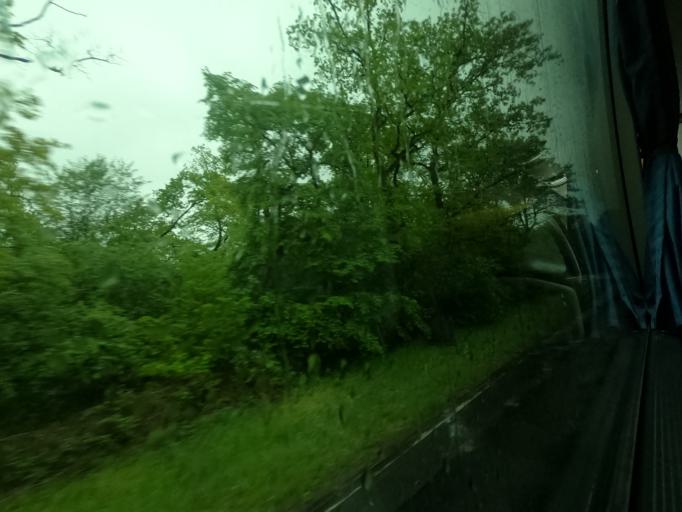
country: DE
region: Hesse
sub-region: Regierungsbezirk Darmstadt
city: Darmstadt
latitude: 49.8714
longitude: 8.6180
